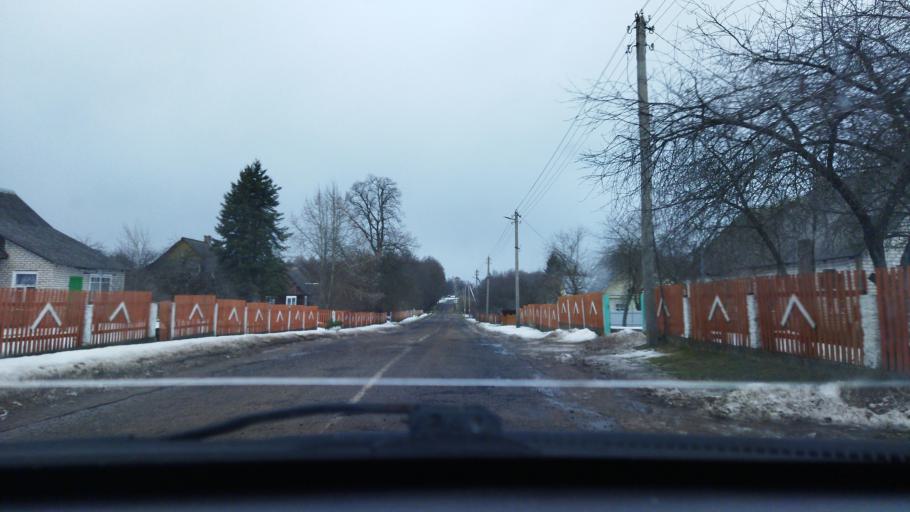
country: BY
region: Minsk
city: Svir
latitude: 54.8971
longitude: 26.4042
